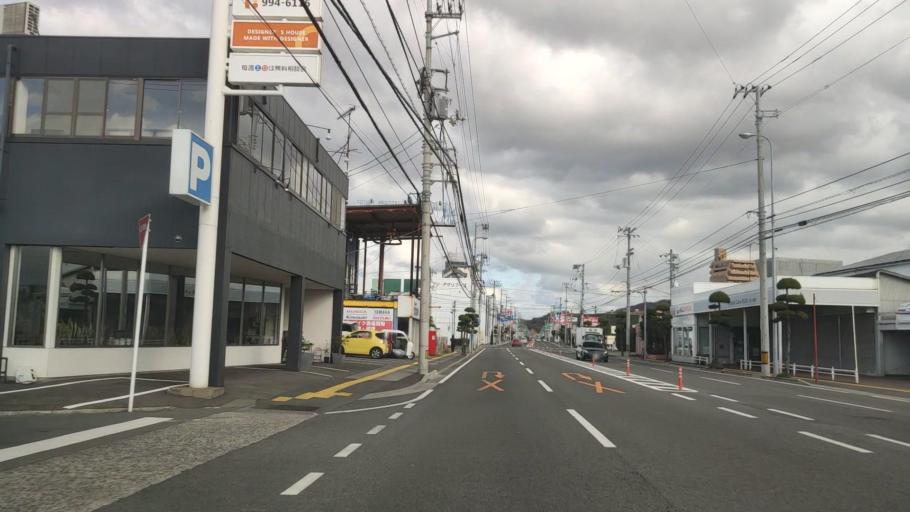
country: JP
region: Ehime
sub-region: Shikoku-chuo Shi
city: Matsuyama
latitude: 33.8599
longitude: 132.7491
